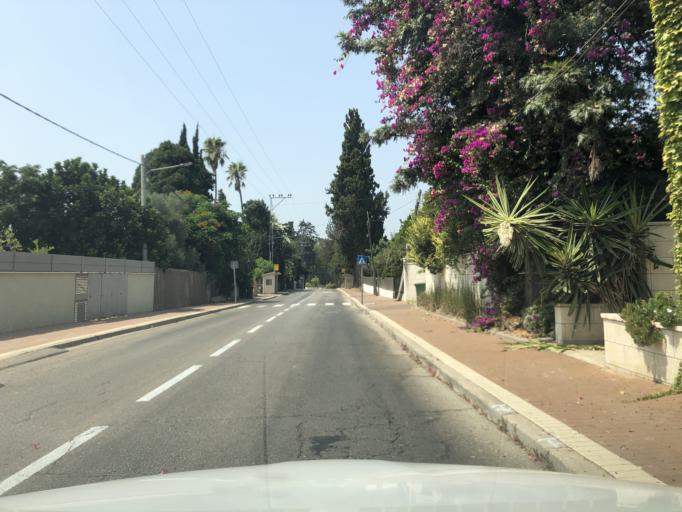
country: IL
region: Central District
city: Ganne Tiqwa
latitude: 32.0686
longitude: 34.8782
